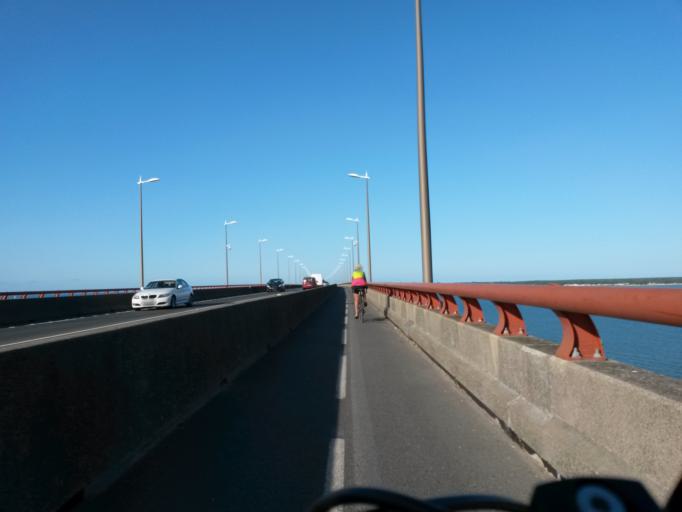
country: FR
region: Poitou-Charentes
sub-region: Departement de la Charente-Maritime
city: Rivedoux-Plage
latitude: 46.1710
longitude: -1.2421
